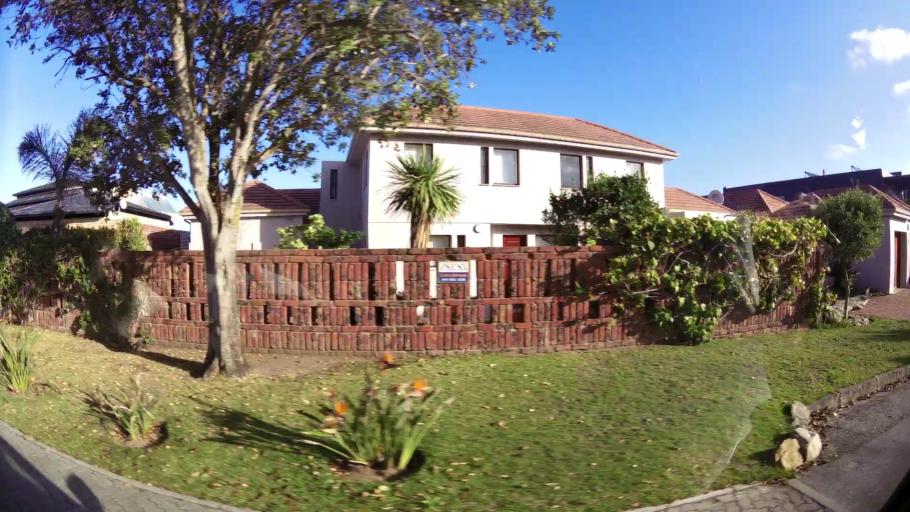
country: ZA
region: Western Cape
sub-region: Eden District Municipality
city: George
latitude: -33.9959
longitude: 22.5885
